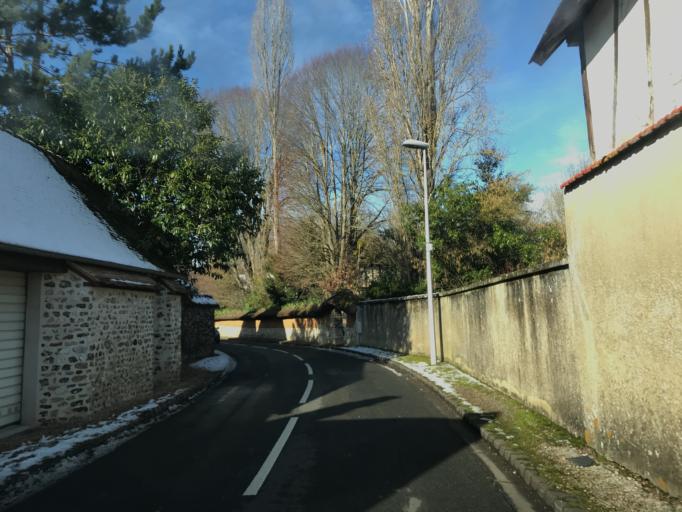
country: FR
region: Haute-Normandie
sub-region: Departement de l'Eure
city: Houlbec-Cocherel
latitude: 49.0688
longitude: 1.2901
